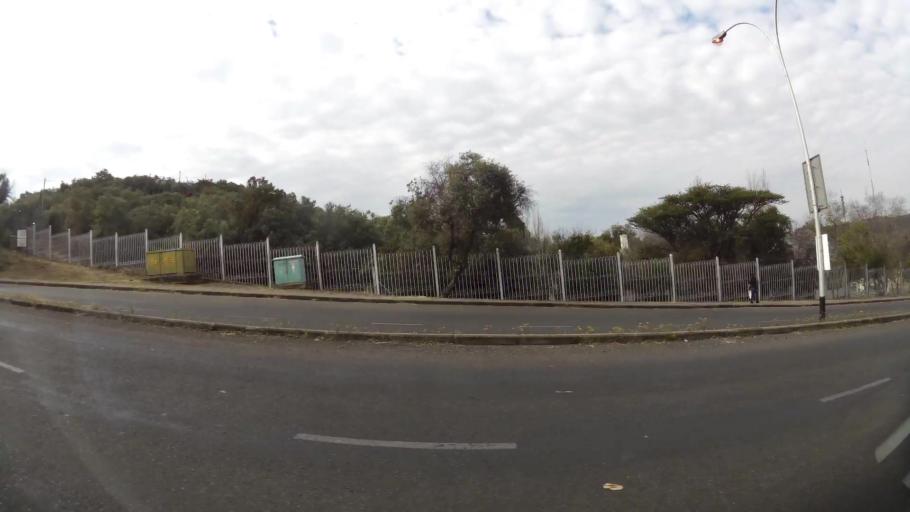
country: ZA
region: Orange Free State
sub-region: Mangaung Metropolitan Municipality
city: Bloemfontein
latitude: -29.0989
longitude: 26.2171
